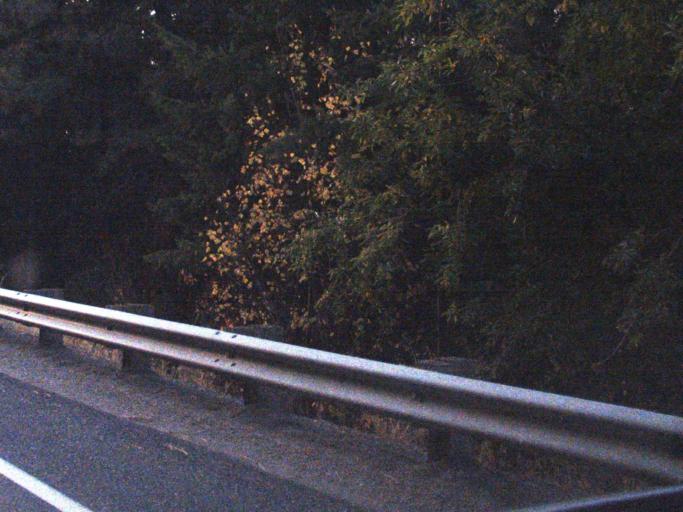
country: US
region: Washington
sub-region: Stevens County
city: Kettle Falls
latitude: 48.6716
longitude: -118.0309
